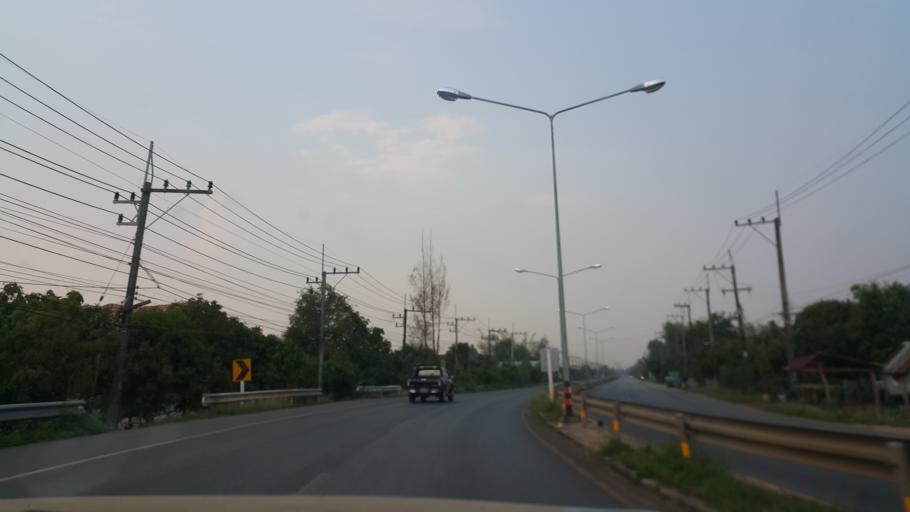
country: TH
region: Nakhon Phanom
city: That Phanom
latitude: 16.9919
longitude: 104.7240
